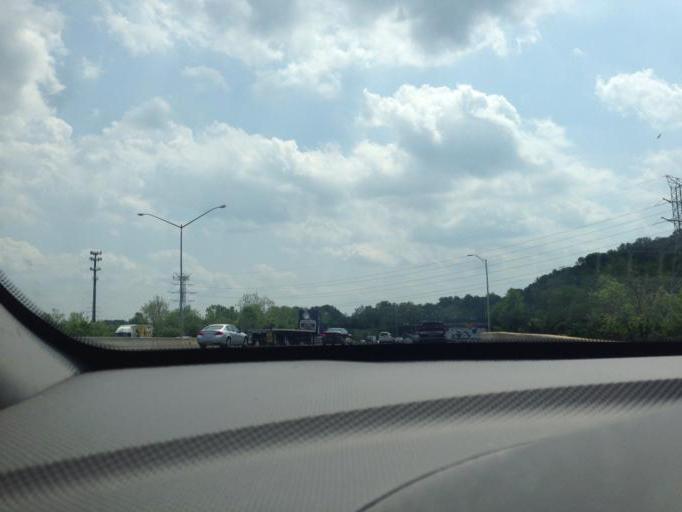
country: US
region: Maryland
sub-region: Baltimore County
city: Mays Chapel
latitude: 39.4110
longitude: -76.6648
